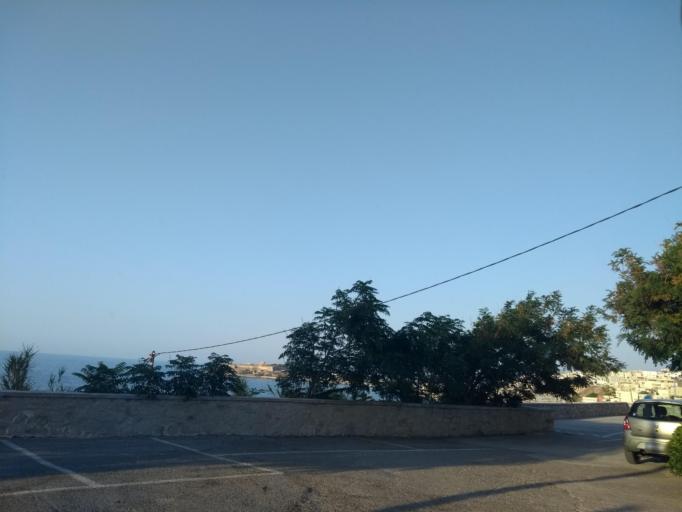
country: GR
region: Crete
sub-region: Nomos Rethymnis
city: Rethymno
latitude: 35.3637
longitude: 24.4539
